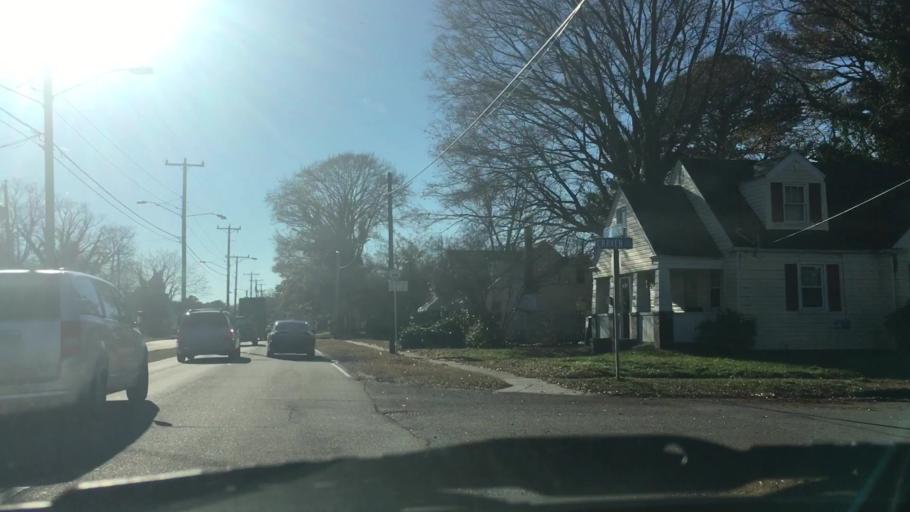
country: US
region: Virginia
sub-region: City of Norfolk
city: Norfolk
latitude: 36.8880
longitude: -76.2417
